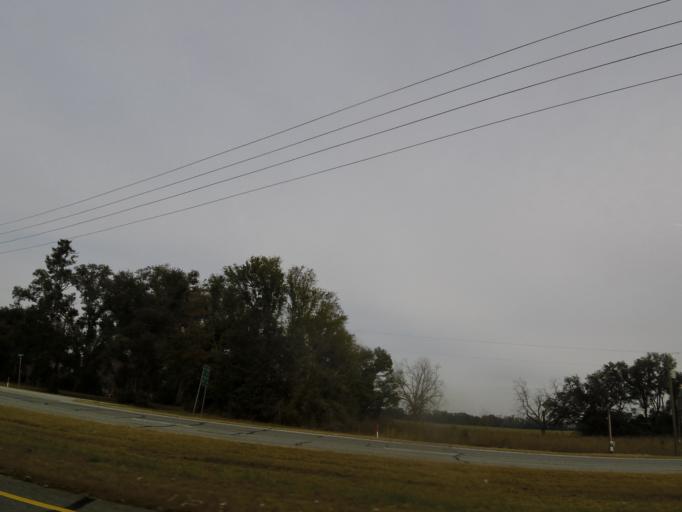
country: US
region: Georgia
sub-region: Seminole County
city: Donalsonville
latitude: 30.9698
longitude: -84.7319
